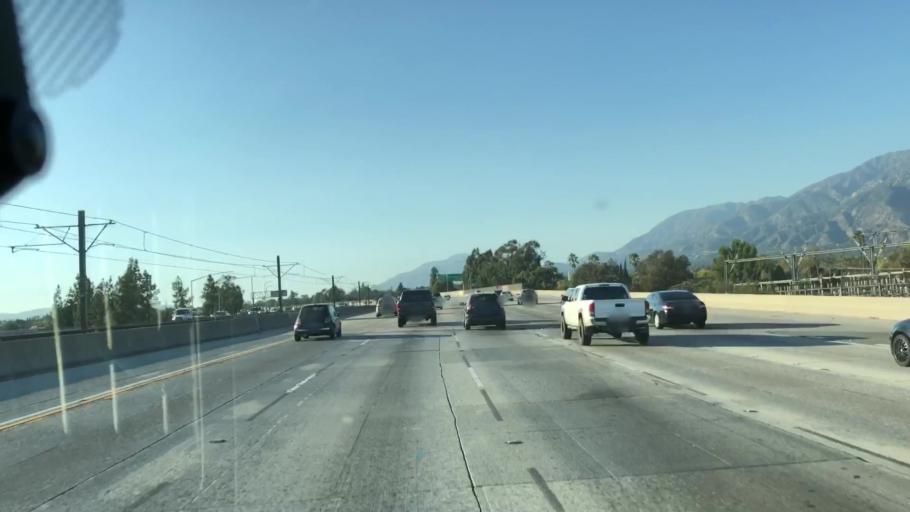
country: US
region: California
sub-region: Los Angeles County
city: East Pasadena
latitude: 34.1496
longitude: -118.0877
